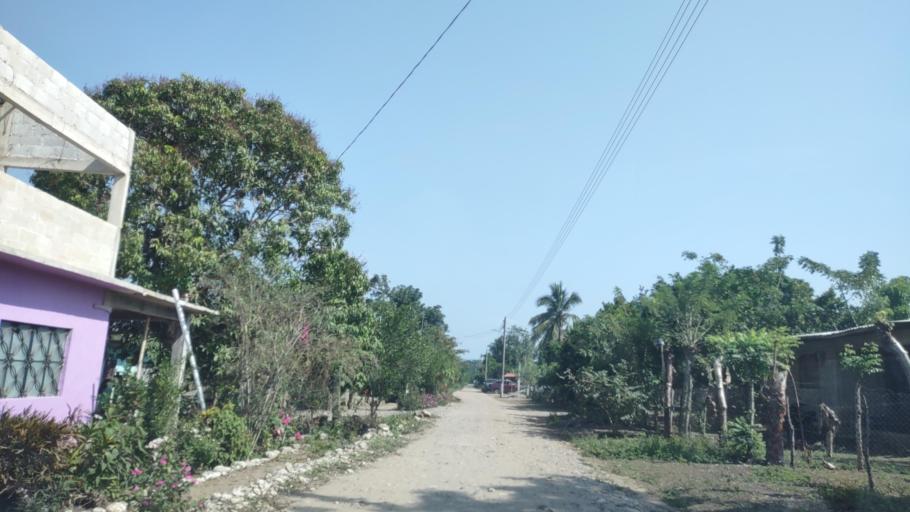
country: MX
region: Puebla
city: Espinal
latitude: 20.2610
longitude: -97.3108
